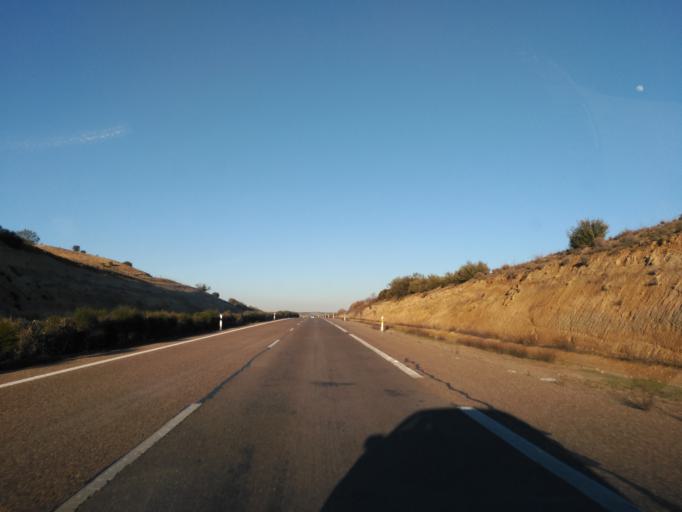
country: ES
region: Castille and Leon
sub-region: Provincia de Zamora
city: Castrillo de la Guarena
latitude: 41.2032
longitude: -5.3344
